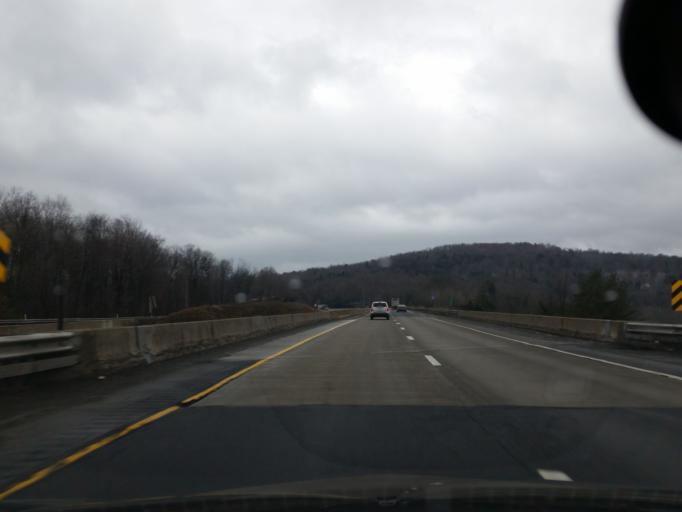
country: US
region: Pennsylvania
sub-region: Lackawanna County
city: Dalton
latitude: 41.6518
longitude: -75.6583
